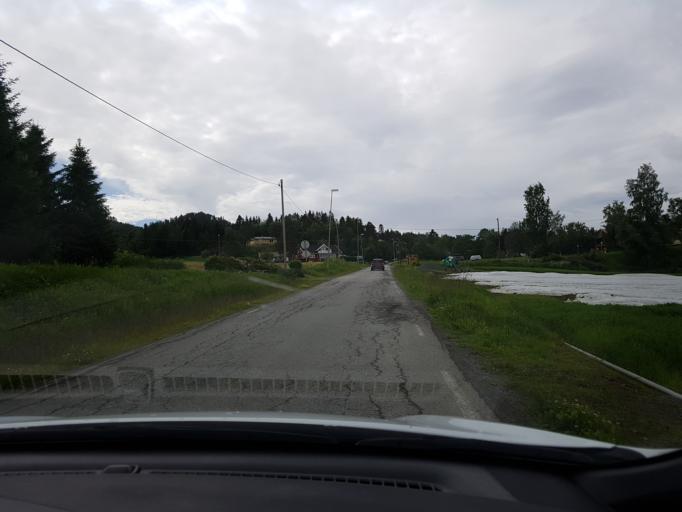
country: NO
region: Nord-Trondelag
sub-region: Frosta
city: Frosta
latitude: 63.6245
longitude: 10.7642
